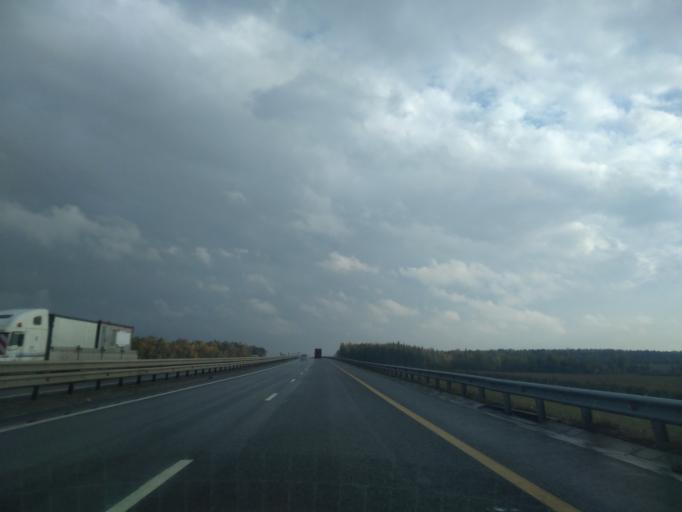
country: RU
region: Lipetsk
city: Yelets
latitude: 52.5989
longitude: 38.6703
